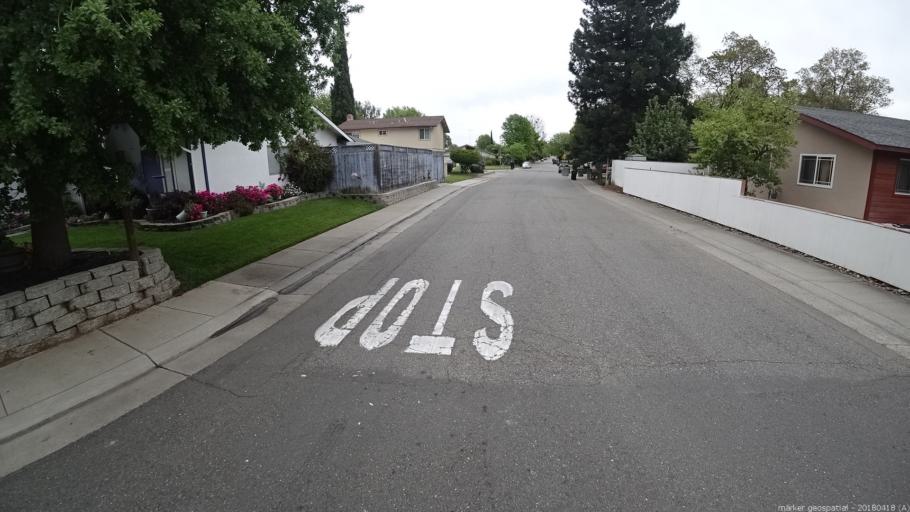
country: US
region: California
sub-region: Sacramento County
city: La Riviera
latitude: 38.5706
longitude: -121.3499
